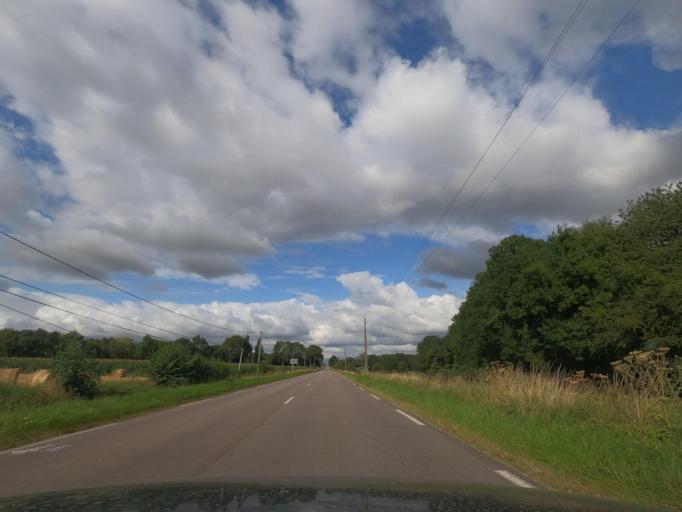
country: FR
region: Haute-Normandie
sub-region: Departement de l'Eure
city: Broglie
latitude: 48.9773
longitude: 0.4889
